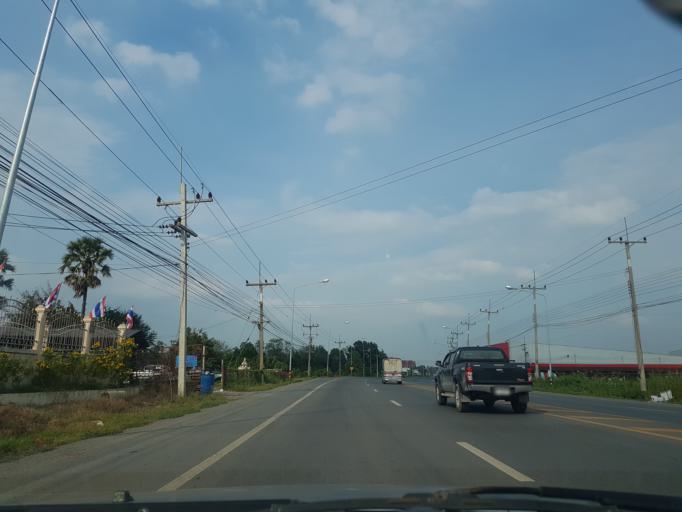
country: TH
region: Sara Buri
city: Ban Mo
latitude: 14.5999
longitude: 100.7345
